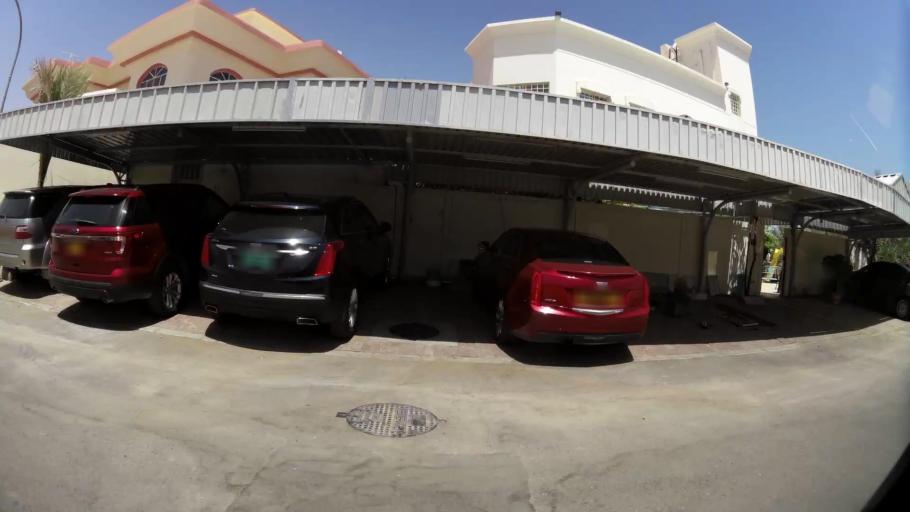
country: OM
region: Muhafazat Masqat
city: Bawshar
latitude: 23.5887
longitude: 58.4493
